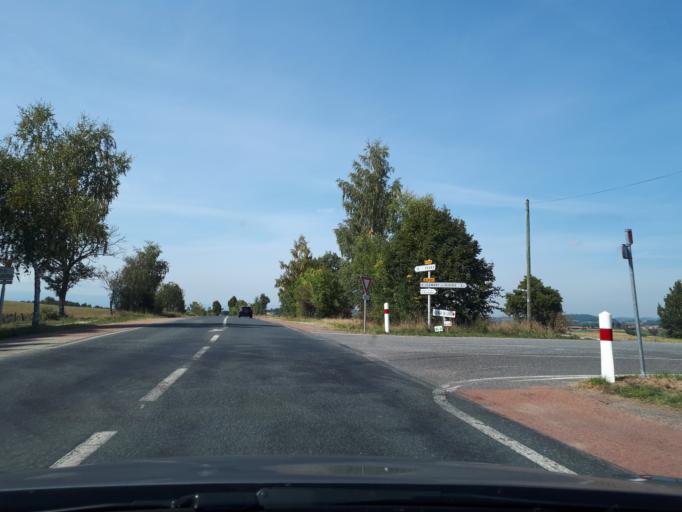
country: FR
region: Rhone-Alpes
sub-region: Departement du Rhone
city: Haute-Rivoire
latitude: 45.7285
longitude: 4.4012
